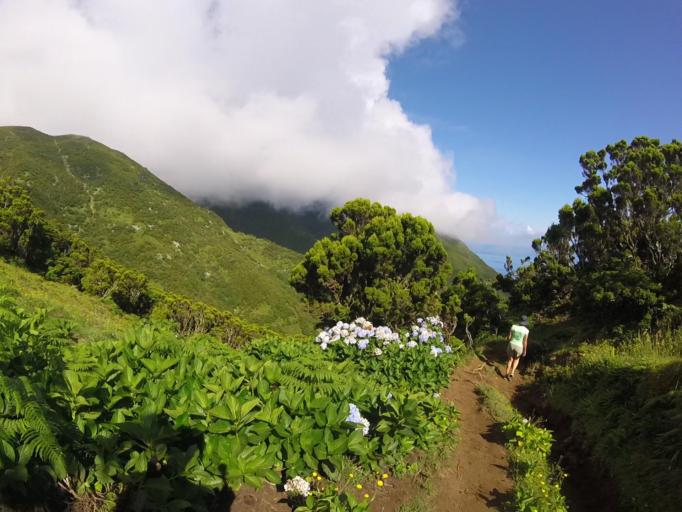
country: PT
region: Azores
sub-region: Sao Roque do Pico
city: Sao Roque do Pico
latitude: 38.6036
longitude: -27.9205
